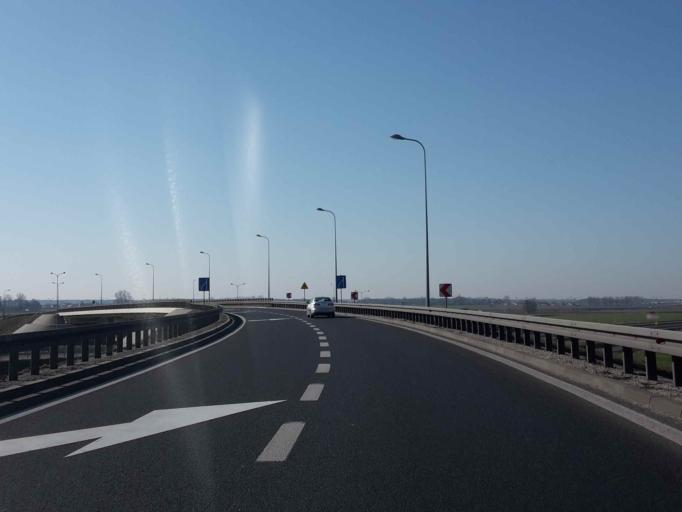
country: PL
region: Greater Poland Voivodeship
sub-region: Powiat gnieznienski
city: Lubowo
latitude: 52.5216
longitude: 17.5030
